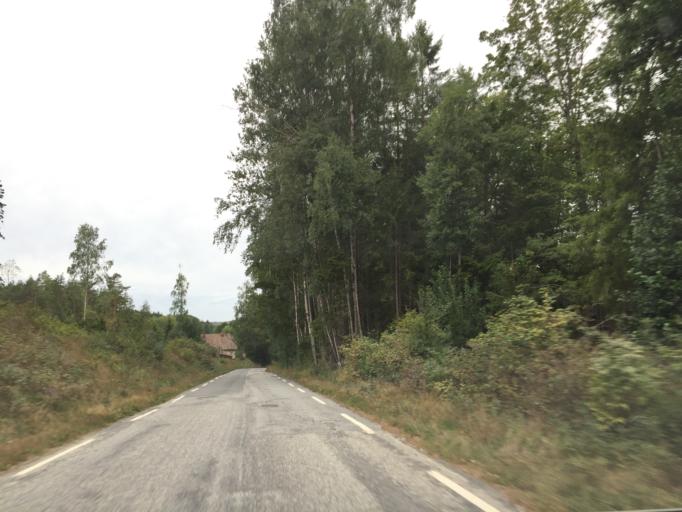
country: NO
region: Ostfold
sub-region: Hvaler
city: Skjaerhalden
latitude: 59.0772
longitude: 11.0114
